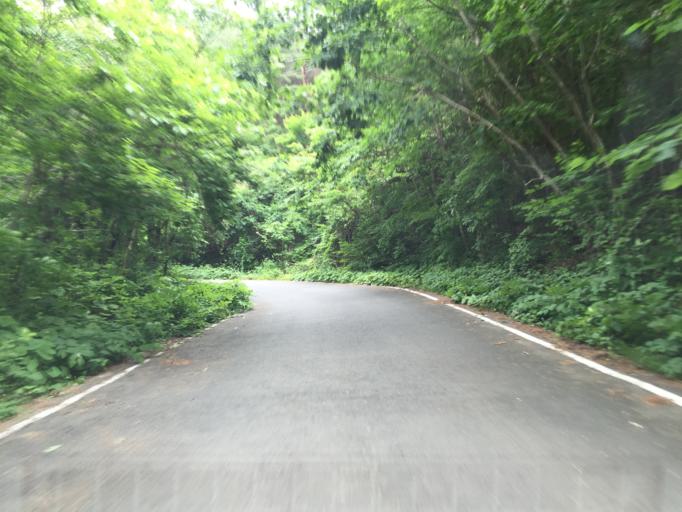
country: JP
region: Fukushima
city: Yanagawamachi-saiwaicho
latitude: 37.7960
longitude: 140.7070
